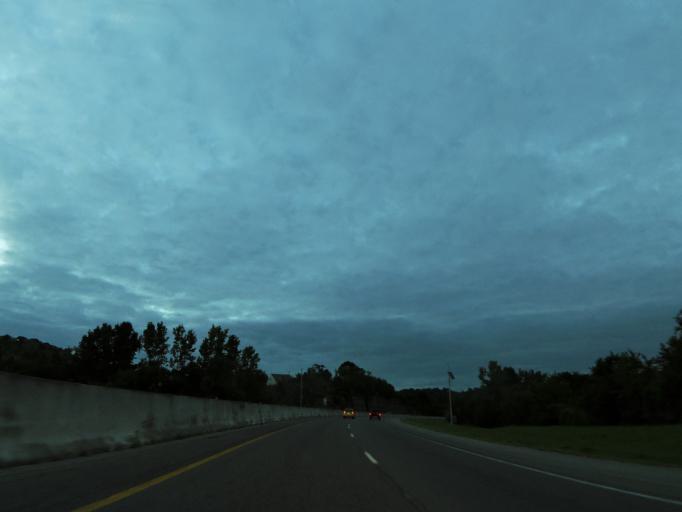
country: US
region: Tennessee
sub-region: Davidson County
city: Nashville
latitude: 36.2208
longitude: -86.8714
